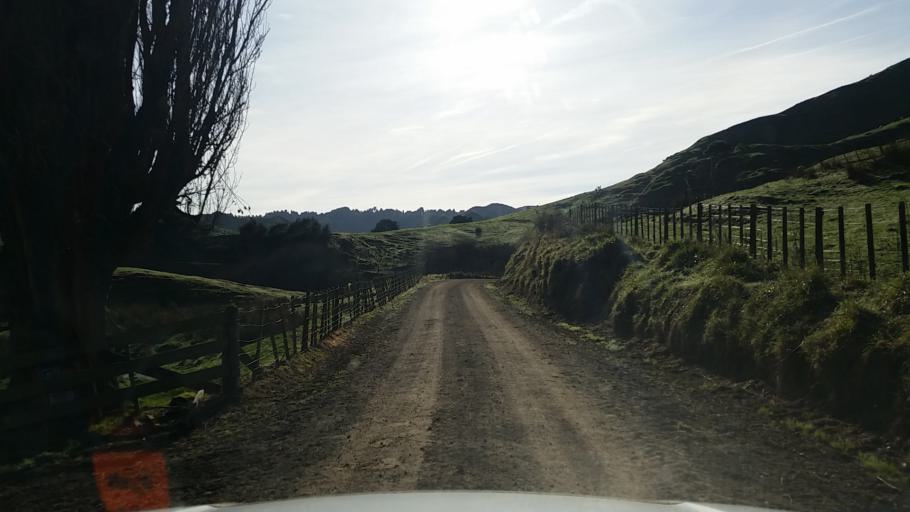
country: NZ
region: Taranaki
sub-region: South Taranaki District
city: Eltham
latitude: -39.3175
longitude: 174.5334
